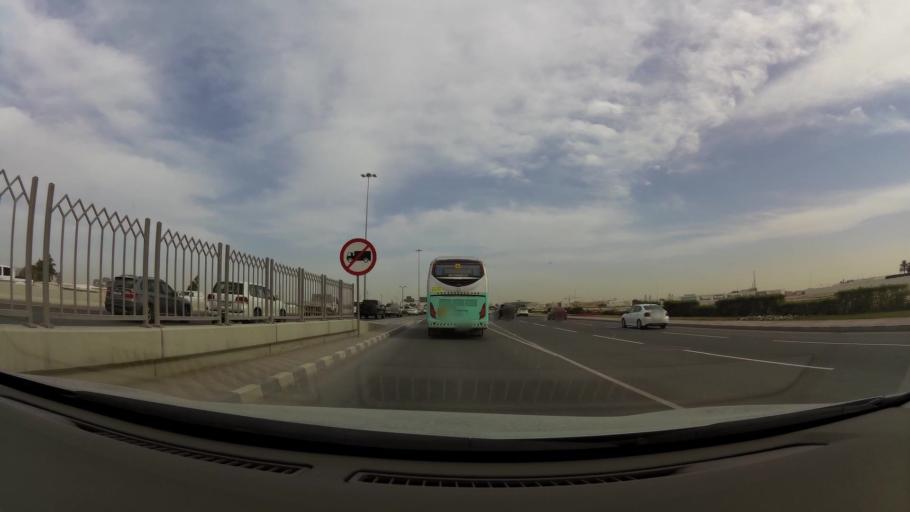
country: QA
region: Baladiyat ad Dawhah
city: Doha
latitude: 25.2858
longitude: 51.4819
